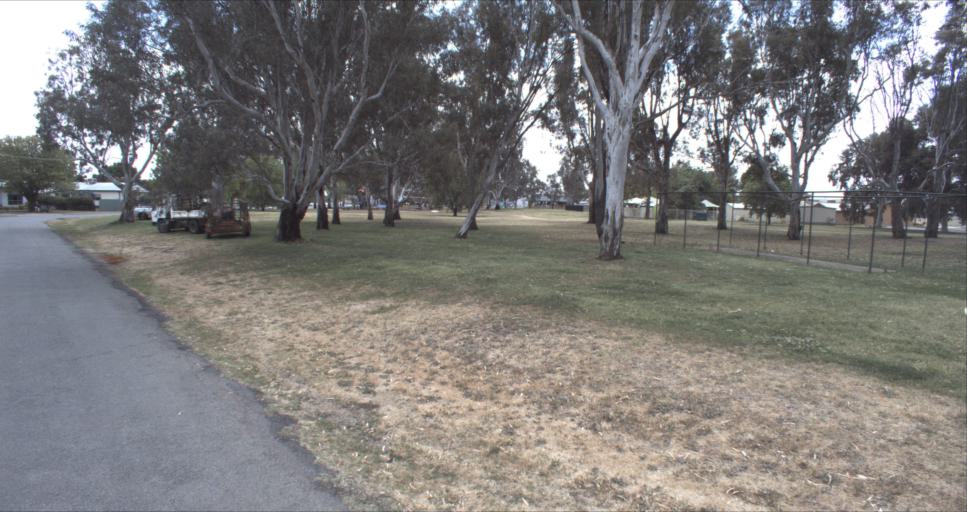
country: AU
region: New South Wales
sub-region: Leeton
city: Leeton
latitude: -34.5558
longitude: 146.3915
